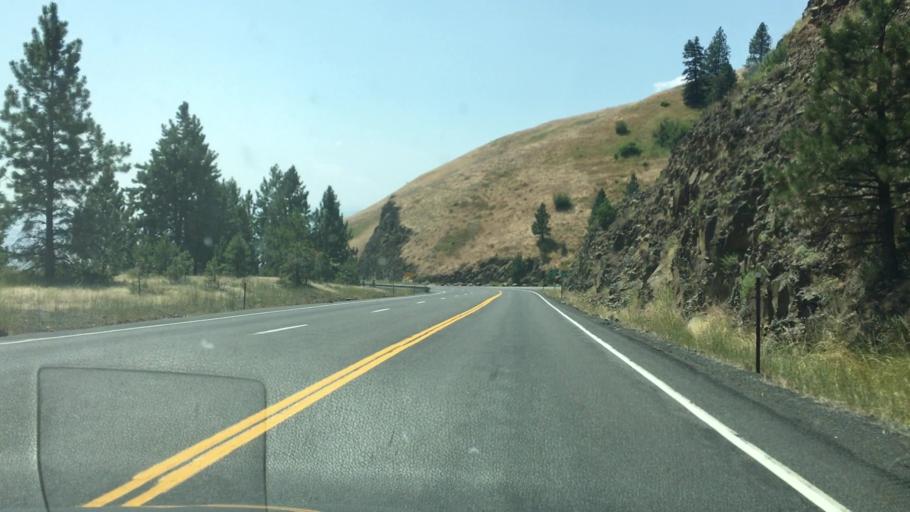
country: US
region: Idaho
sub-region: Idaho County
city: Grangeville
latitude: 45.8393
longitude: -116.2380
